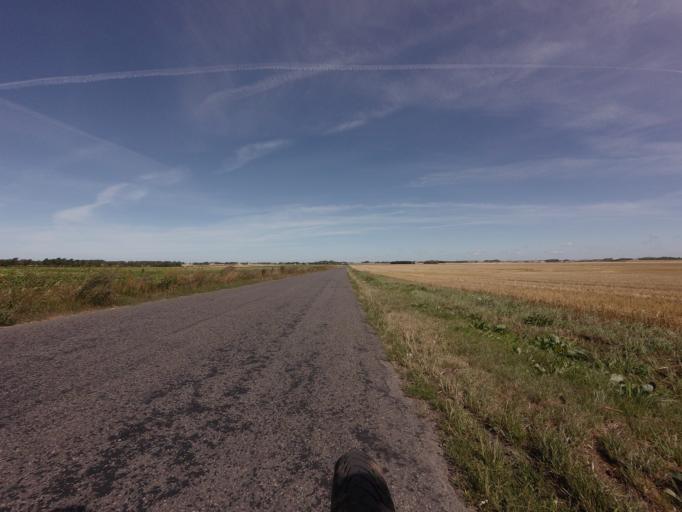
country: DK
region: North Denmark
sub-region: Bronderslev Kommune
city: Bronderslev
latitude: 57.3085
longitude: 9.8090
